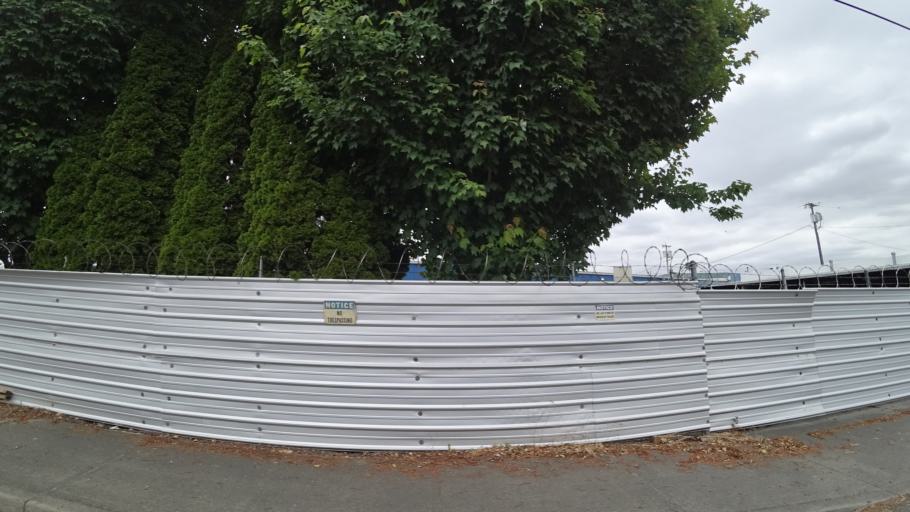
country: US
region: Washington
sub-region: Clark County
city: Vancouver
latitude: 45.5906
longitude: -122.7021
